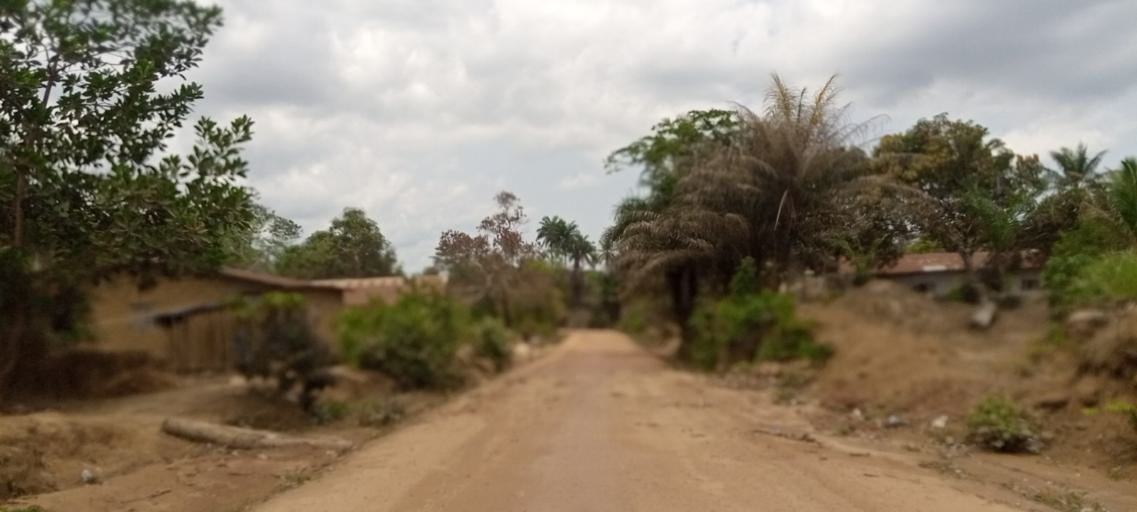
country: SL
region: Western Area
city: Waterloo
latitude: 8.3154
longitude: -13.0044
